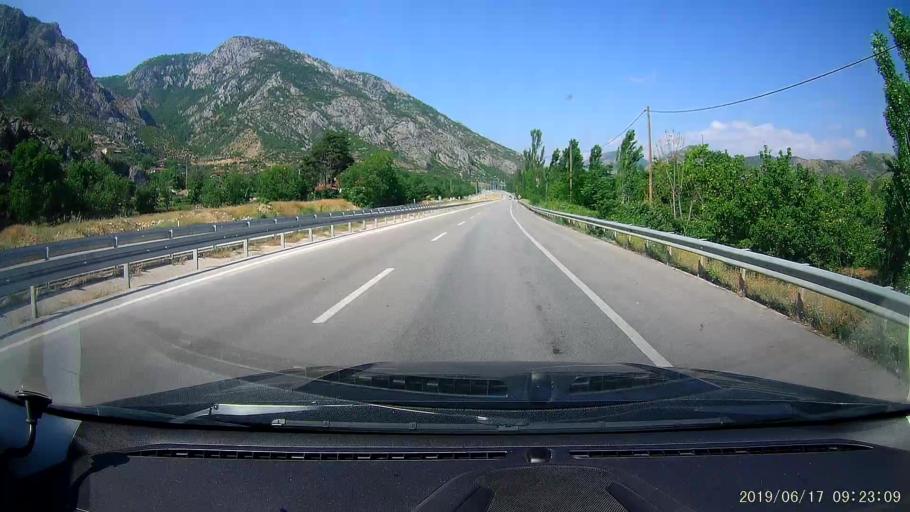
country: TR
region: Amasya
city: Amasya
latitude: 40.6788
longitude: 35.8800
